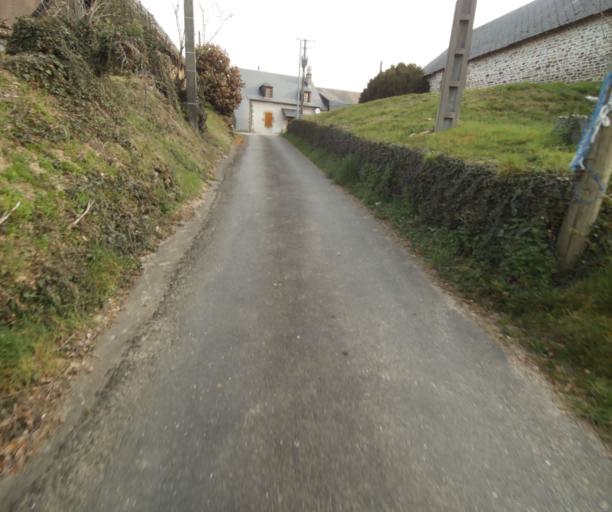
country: FR
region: Limousin
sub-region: Departement de la Correze
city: Chamboulive
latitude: 45.4322
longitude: 1.7950
